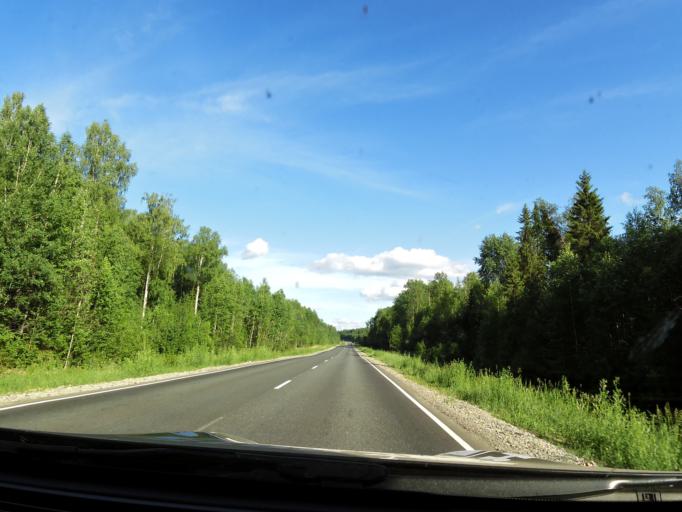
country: RU
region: Kirov
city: Chernaya Kholunitsa
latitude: 58.7814
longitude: 51.9120
